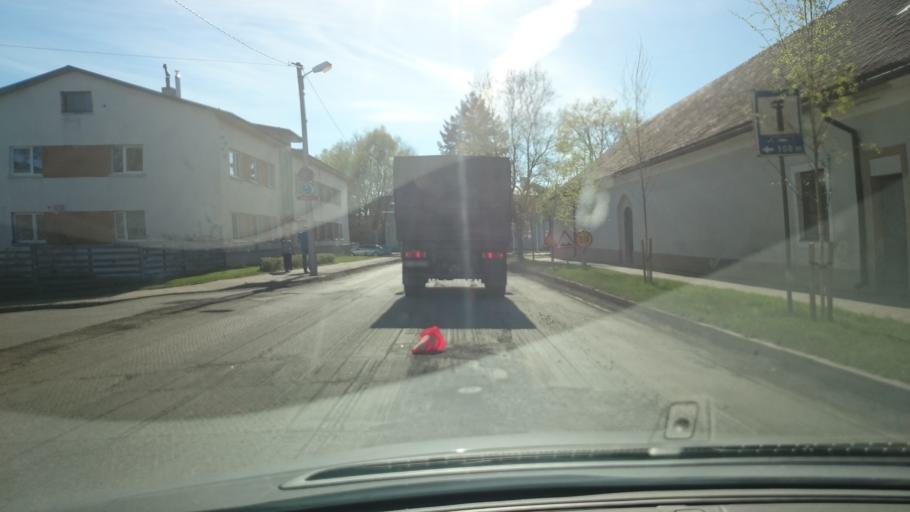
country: EE
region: Laeaene-Virumaa
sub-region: Rakvere linn
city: Rakvere
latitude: 59.3497
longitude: 26.3502
